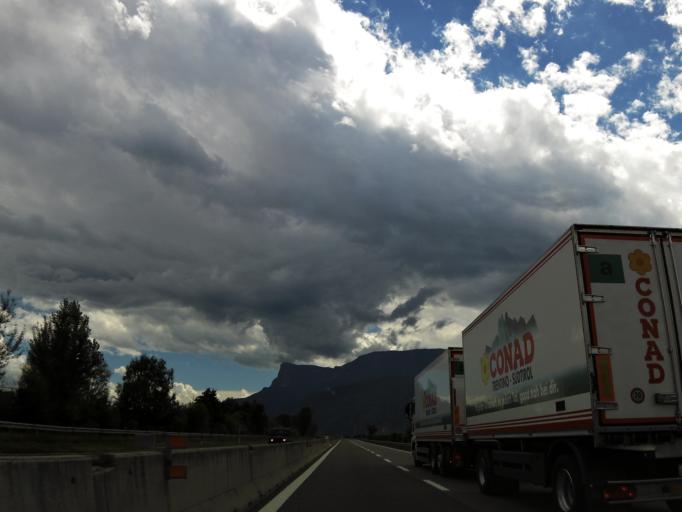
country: IT
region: Trentino-Alto Adige
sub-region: Bolzano
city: Postal
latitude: 46.5951
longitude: 11.1864
